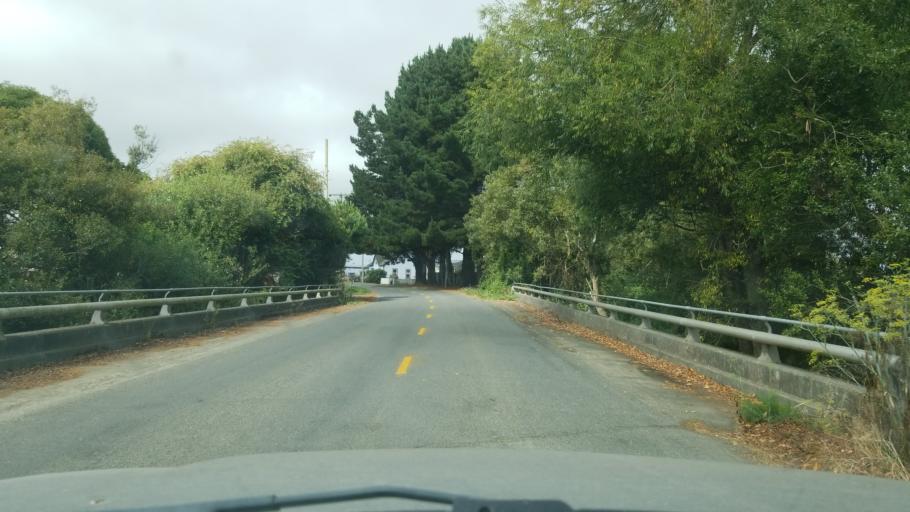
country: US
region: California
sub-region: Humboldt County
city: Ferndale
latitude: 40.5946
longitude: -124.2535
